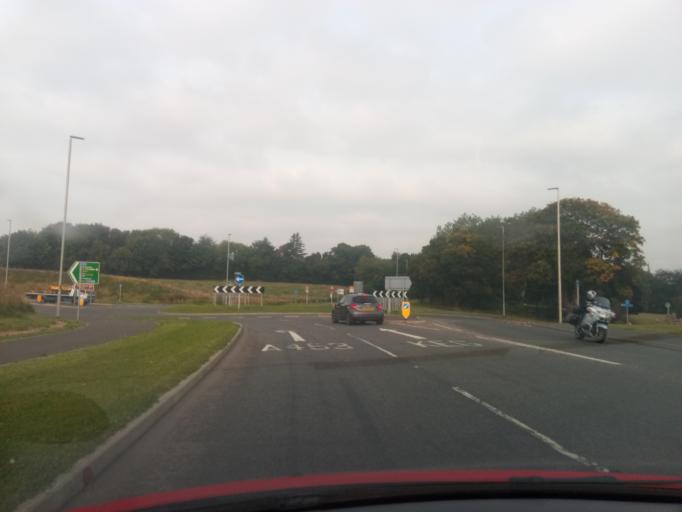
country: GB
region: England
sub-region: Leicestershire
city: Kegworth
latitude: 52.8319
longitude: -1.2909
